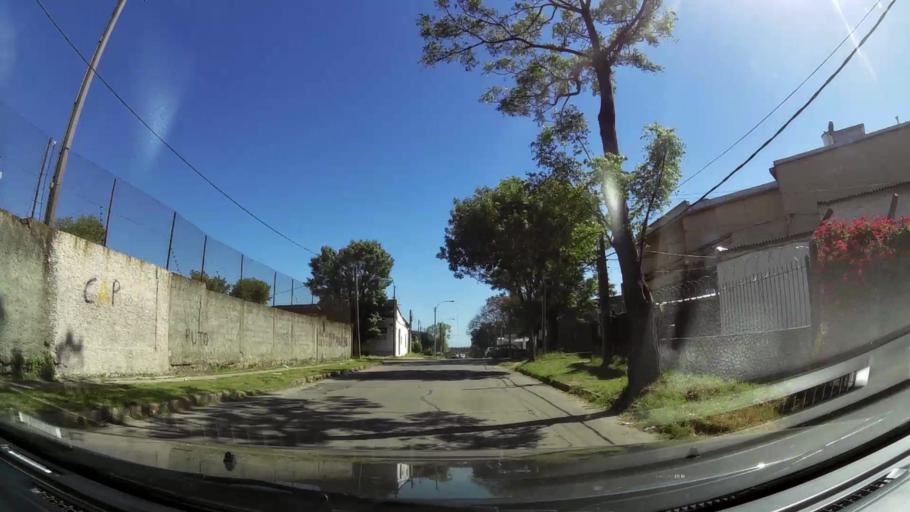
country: UY
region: Montevideo
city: Montevideo
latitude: -34.8690
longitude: -56.1288
